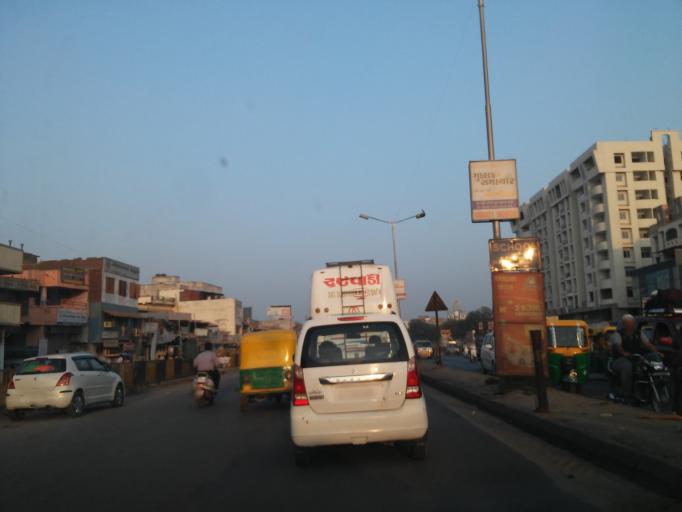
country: IN
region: Gujarat
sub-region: Ahmadabad
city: Sarkhej
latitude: 22.9934
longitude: 72.5250
